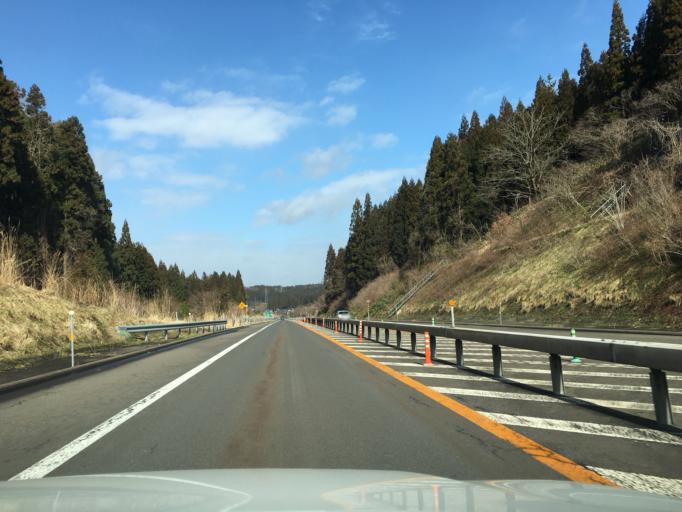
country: JP
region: Akita
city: Akita
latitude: 39.7316
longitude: 140.1779
